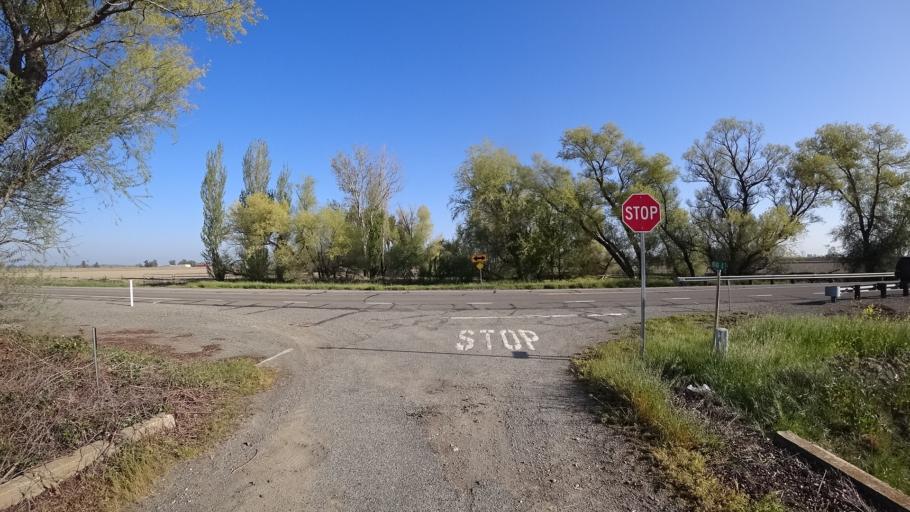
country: US
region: California
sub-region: Glenn County
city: Willows
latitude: 39.5237
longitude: -122.1263
